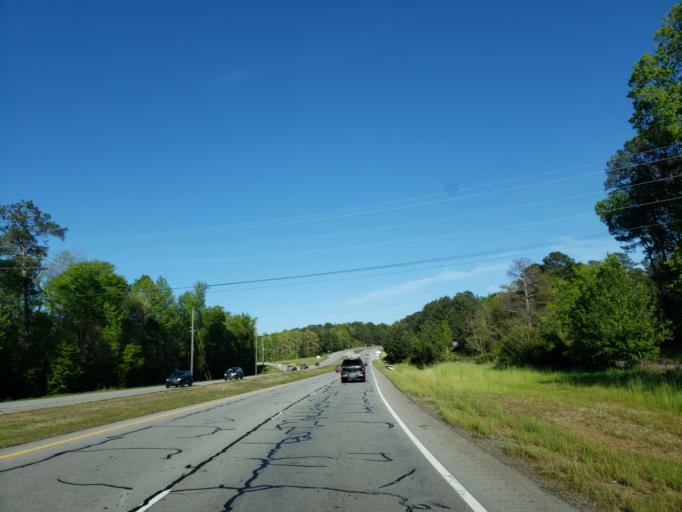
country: US
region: Georgia
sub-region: Paulding County
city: Dallas
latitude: 33.9186
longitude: -84.8732
